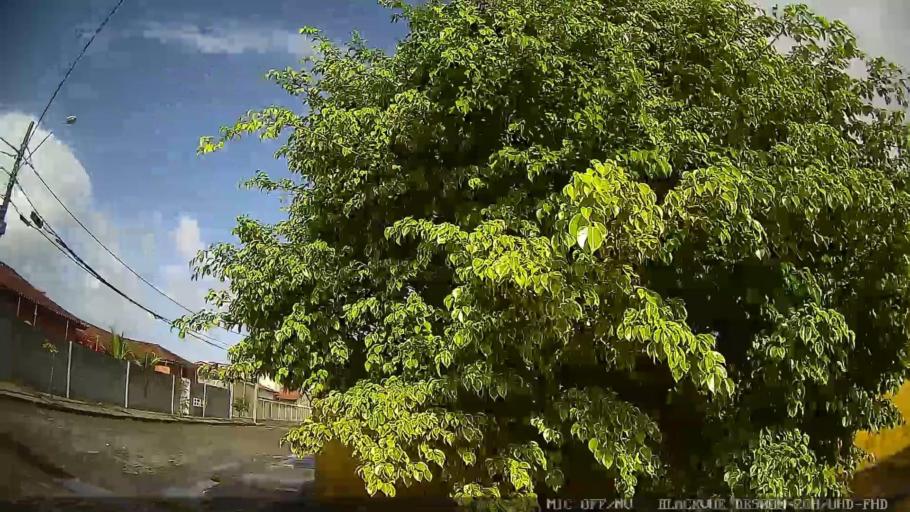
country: BR
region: Sao Paulo
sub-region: Itanhaem
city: Itanhaem
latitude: -24.2100
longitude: -46.8378
